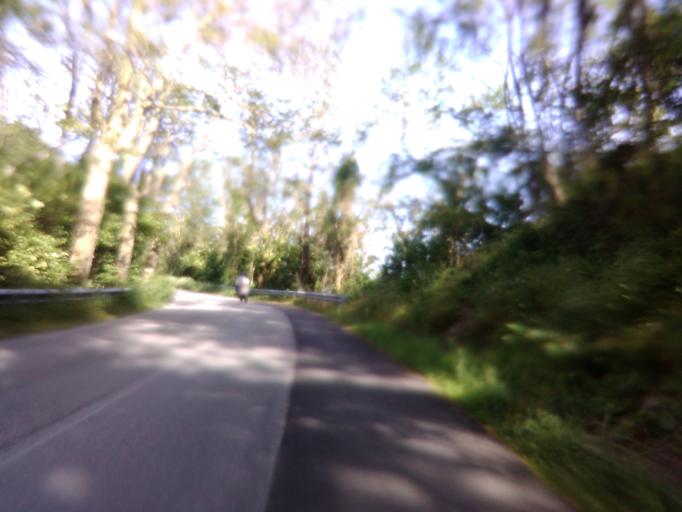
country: IT
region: Tuscany
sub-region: Provincia di Massa-Carrara
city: Fosdinovo
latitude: 44.1219
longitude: 10.0536
